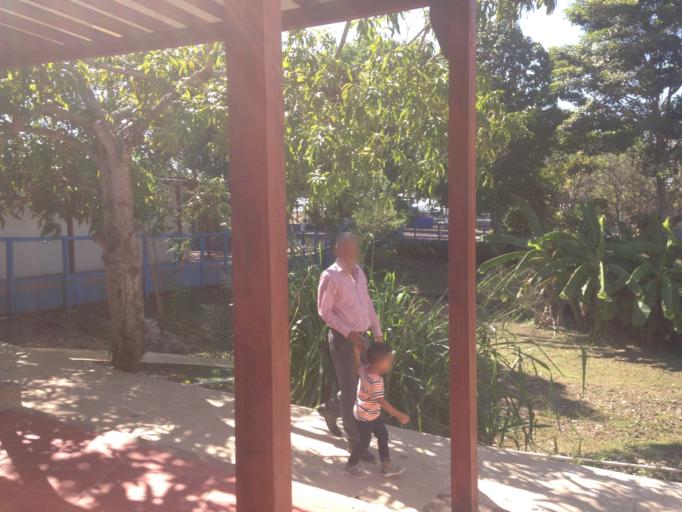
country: CO
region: Atlantico
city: Baranoa
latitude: 10.8405
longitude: -74.9016
